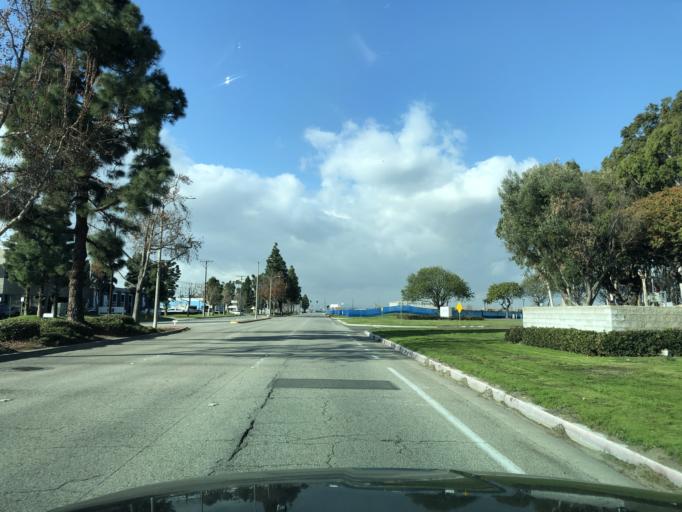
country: US
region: California
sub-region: Orange County
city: Westminster
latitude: 33.7445
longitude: -118.0353
